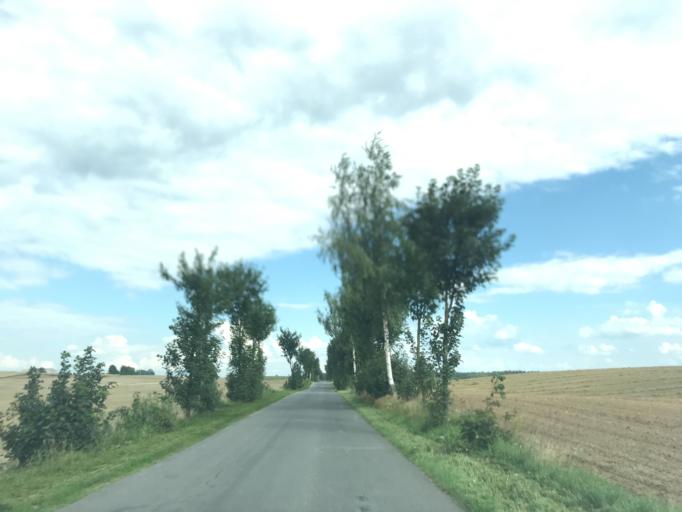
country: PL
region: Kujawsko-Pomorskie
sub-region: Powiat brodnicki
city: Brzozie
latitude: 53.3294
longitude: 19.6712
